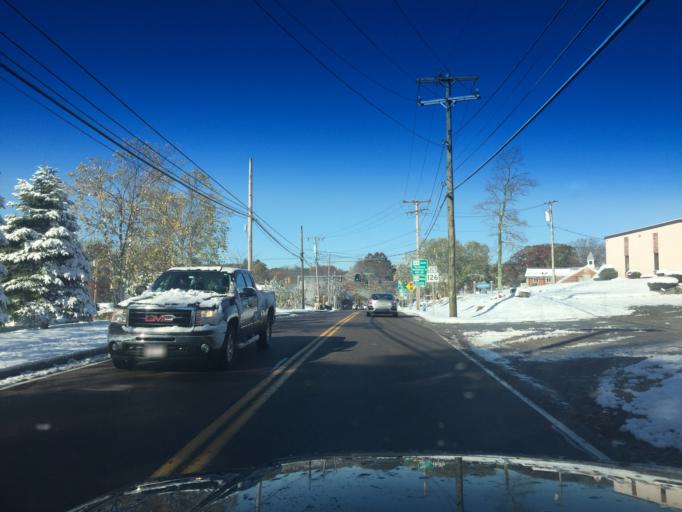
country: US
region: Massachusetts
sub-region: Norfolk County
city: Medway
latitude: 42.1445
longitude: -71.4415
